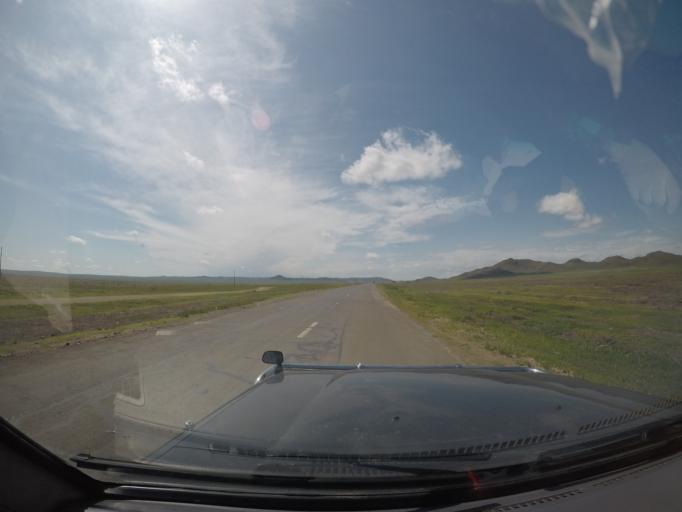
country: MN
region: Hentiy
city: Moron
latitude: 47.3791
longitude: 110.4210
